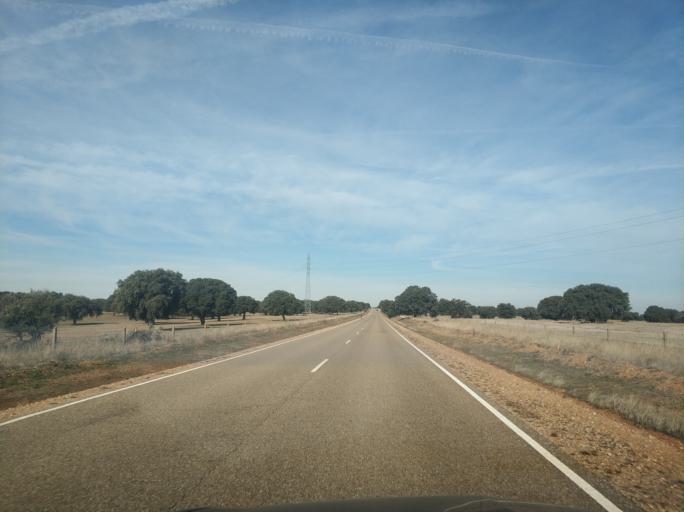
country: ES
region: Castille and Leon
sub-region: Provincia de Salamanca
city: Parada de Arriba
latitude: 40.9974
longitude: -5.8227
